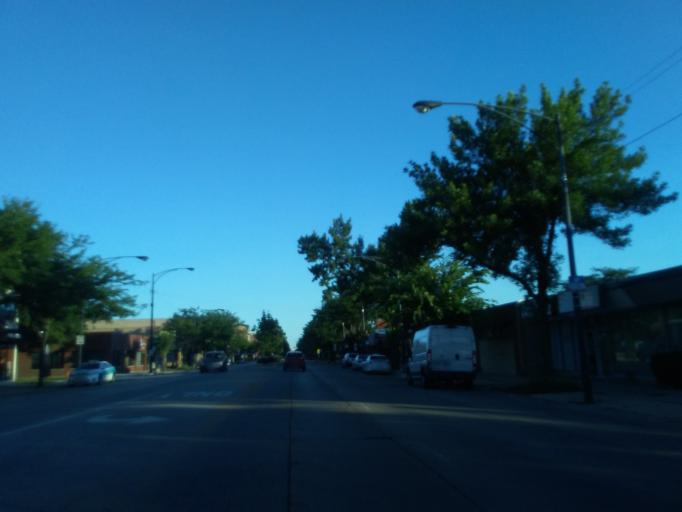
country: US
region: Illinois
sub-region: Cook County
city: Lincolnwood
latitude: 41.9866
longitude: -87.7009
